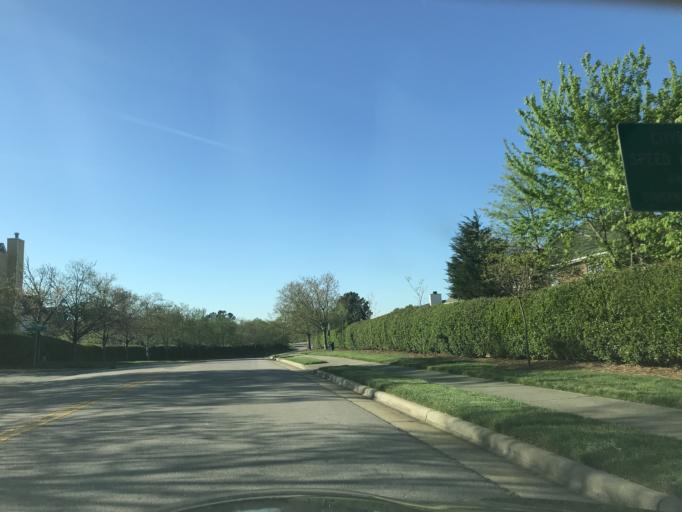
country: US
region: North Carolina
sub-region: Wake County
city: Knightdale
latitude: 35.8342
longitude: -78.5607
